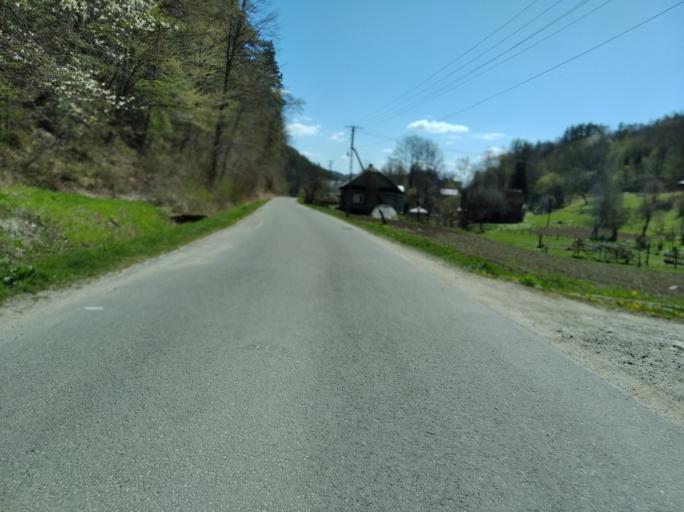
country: PL
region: Subcarpathian Voivodeship
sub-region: Powiat brzozowski
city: Dydnia
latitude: 49.7144
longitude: 22.1914
